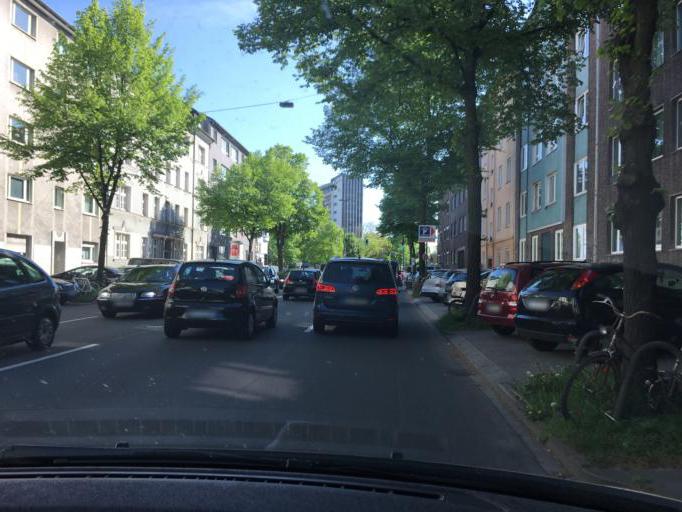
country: DE
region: North Rhine-Westphalia
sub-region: Regierungsbezirk Dusseldorf
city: Dusseldorf
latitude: 51.2028
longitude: 6.7765
